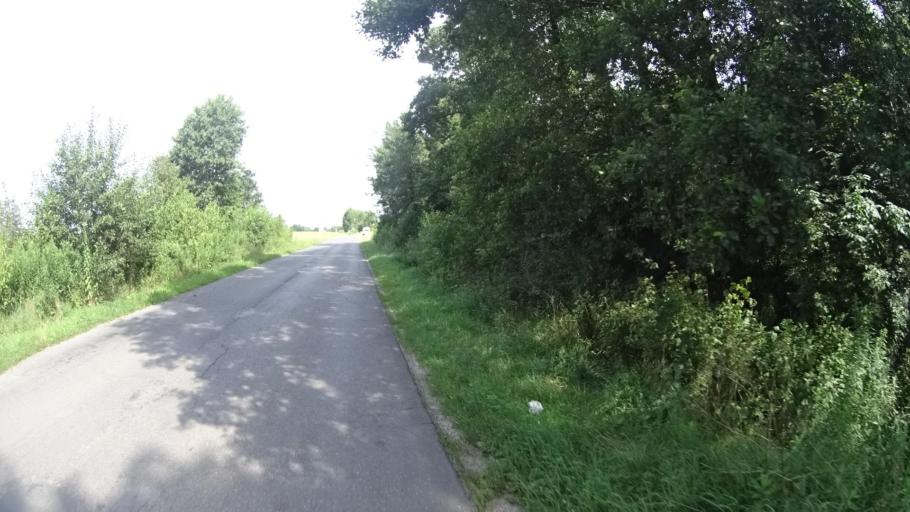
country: PL
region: Masovian Voivodeship
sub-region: Powiat piaseczynski
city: Tarczyn
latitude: 52.0118
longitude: 20.8023
